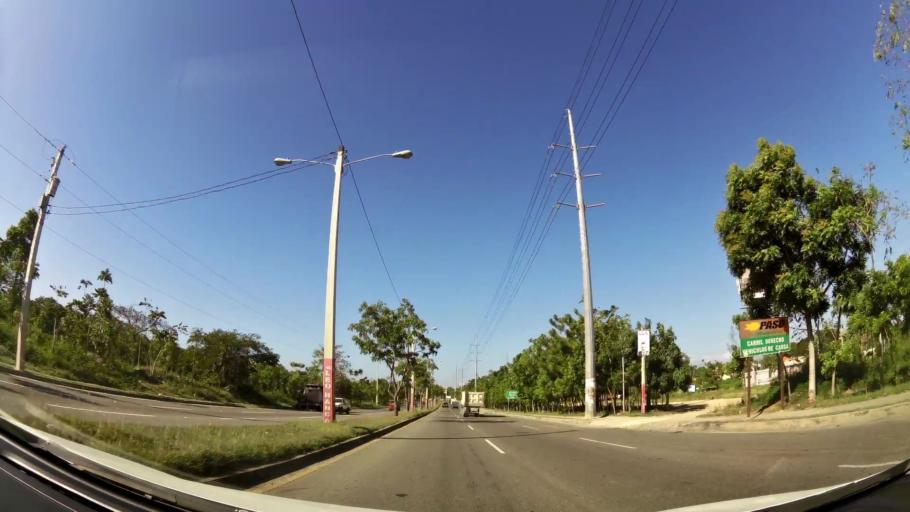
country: DO
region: San Cristobal
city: El Carril
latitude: 18.4469
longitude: -69.9964
